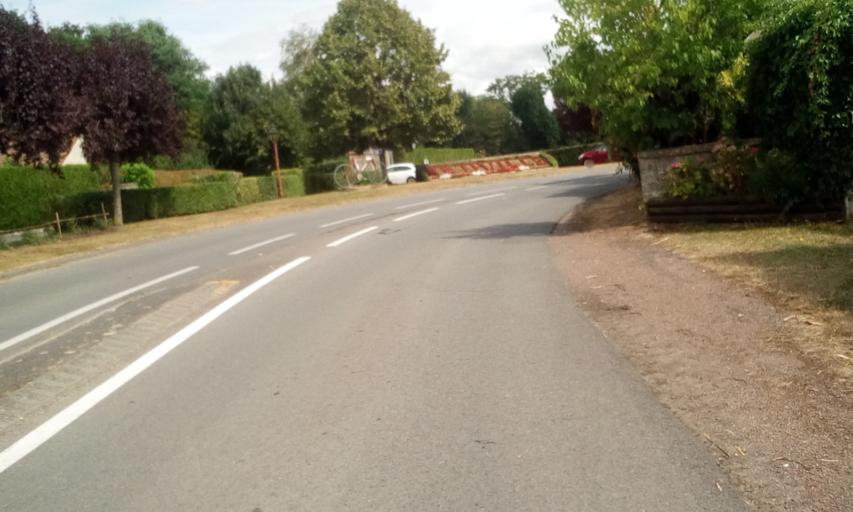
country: FR
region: Lower Normandy
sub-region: Departement du Calvados
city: Bavent
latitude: 49.2418
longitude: -0.1797
